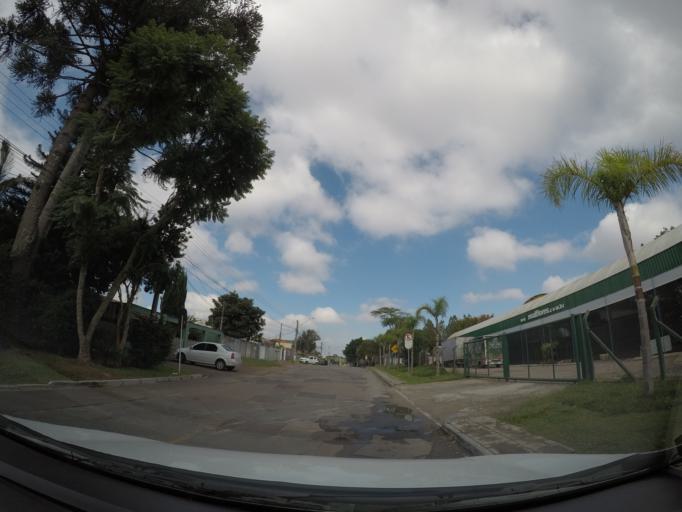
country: BR
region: Parana
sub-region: Sao Jose Dos Pinhais
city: Sao Jose dos Pinhais
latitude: -25.4913
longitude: -49.2228
